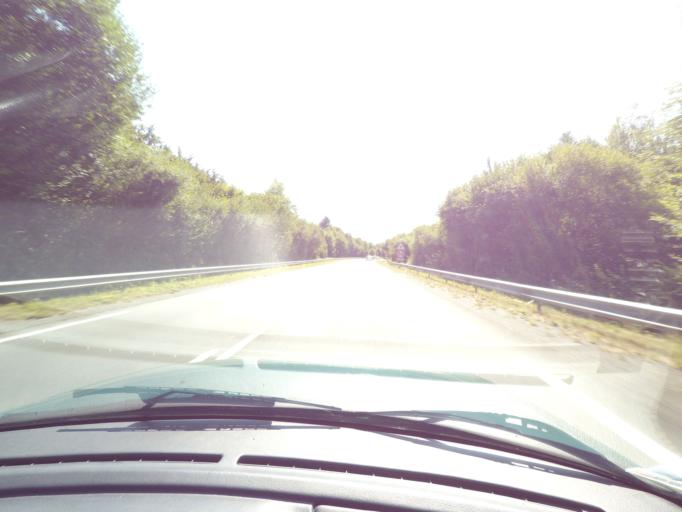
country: FR
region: Limousin
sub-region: Departement de la Haute-Vienne
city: Chaptelat
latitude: 45.8973
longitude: 1.2434
